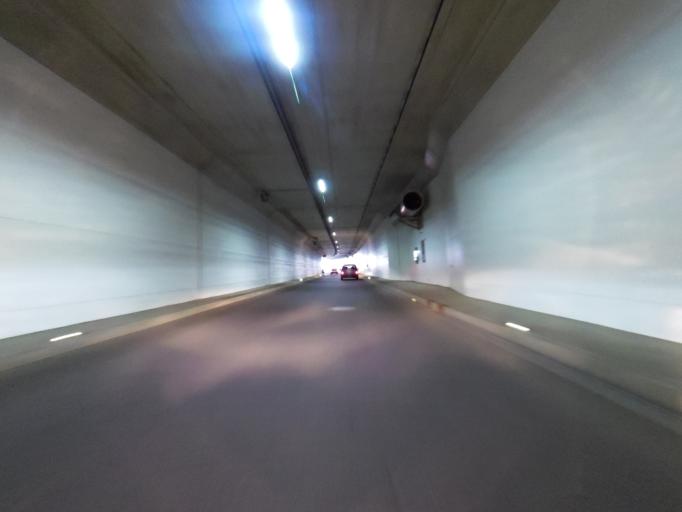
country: DE
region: Saxony
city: Albertstadt
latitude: 51.0672
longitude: 13.7784
